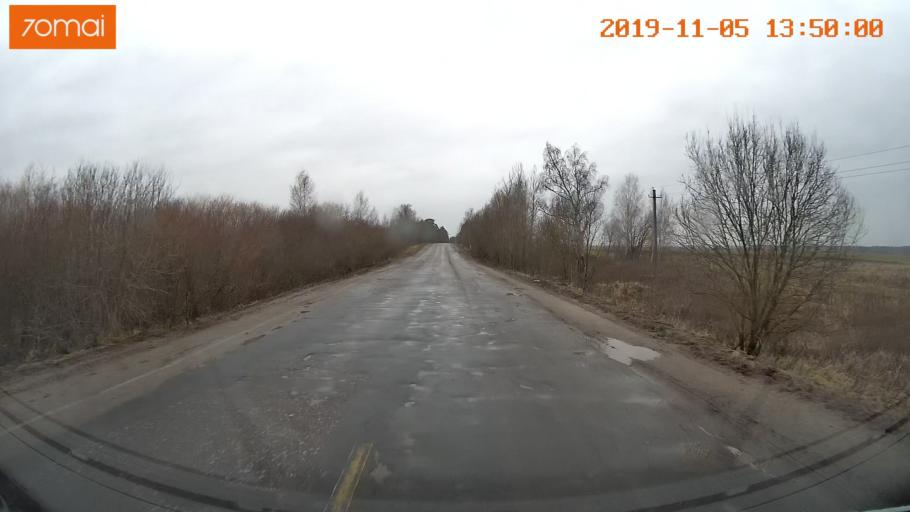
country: RU
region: Ivanovo
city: Kaminskiy
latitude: 57.0159
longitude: 41.4103
